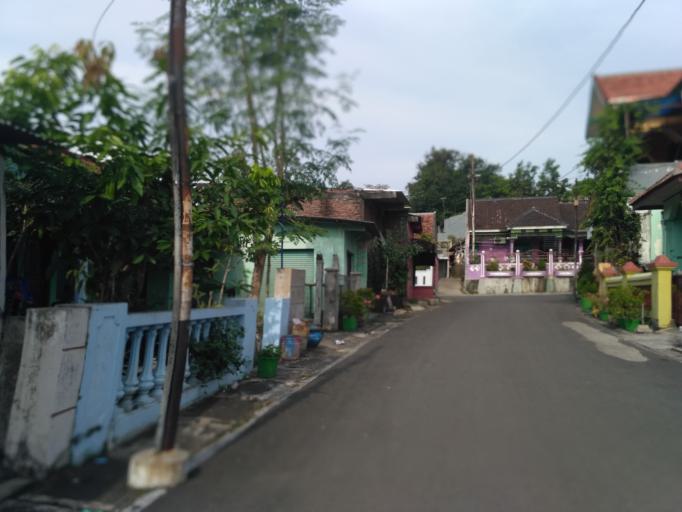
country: ID
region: Central Java
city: Semarang
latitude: -7.0171
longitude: 110.4499
